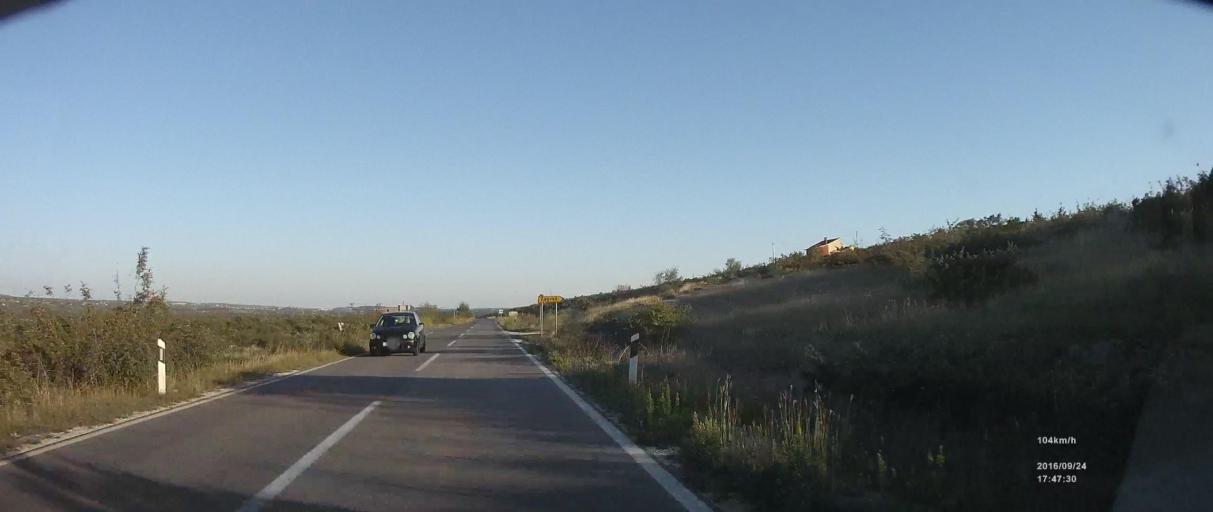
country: HR
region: Zadarska
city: Polaca
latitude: 44.0746
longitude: 15.5237
